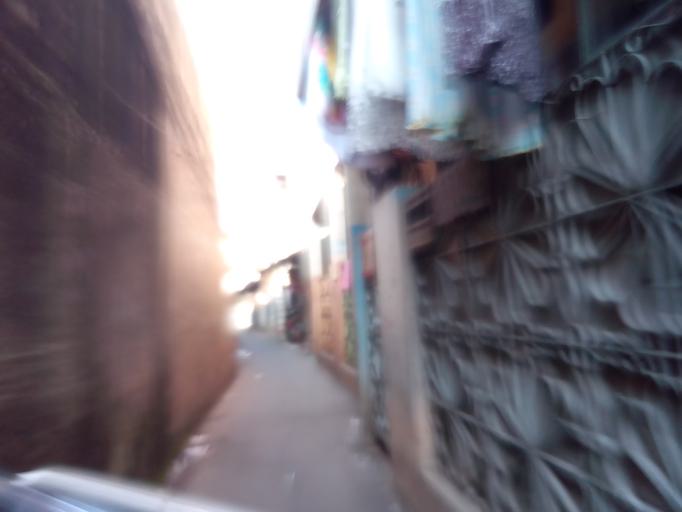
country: ID
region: Jakarta Raya
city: Jakarta
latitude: -6.2655
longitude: 106.8116
